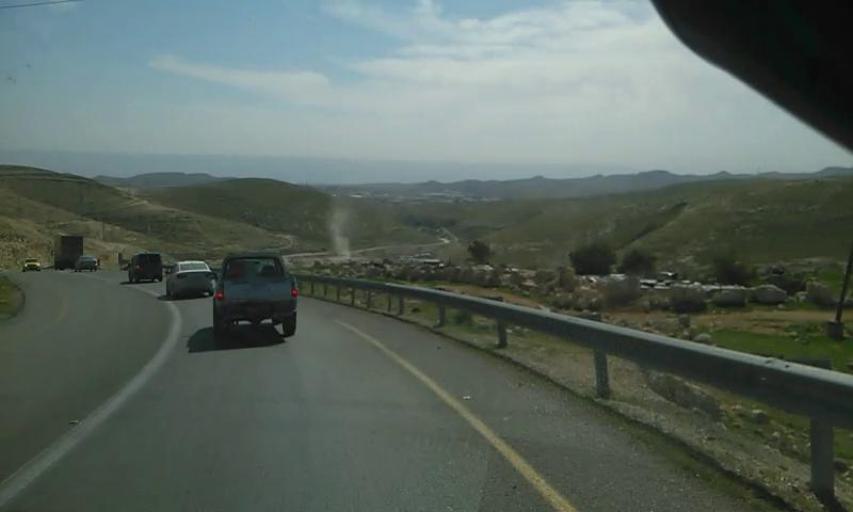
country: PS
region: West Bank
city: `Anata
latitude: 31.8120
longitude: 35.2987
